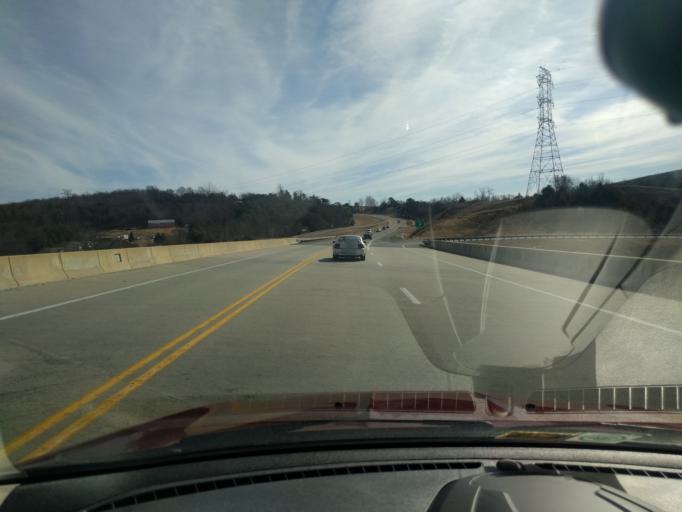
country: US
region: Virginia
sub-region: City of Staunton
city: Staunton
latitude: 38.1324
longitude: -79.0935
